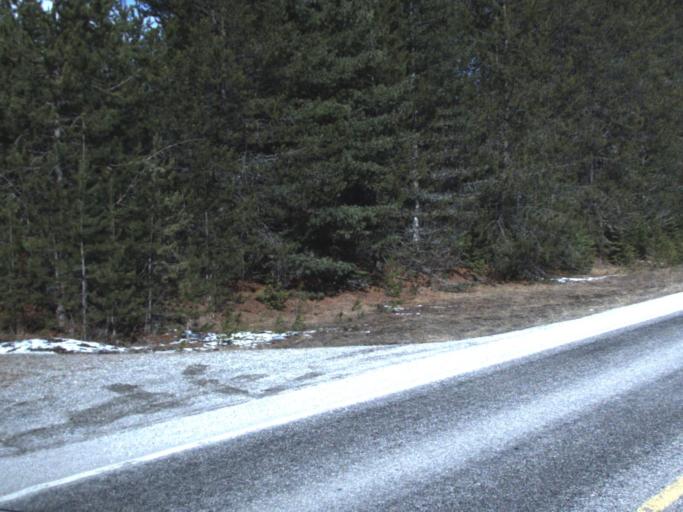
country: CA
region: British Columbia
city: Fruitvale
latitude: 48.6804
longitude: -117.4031
